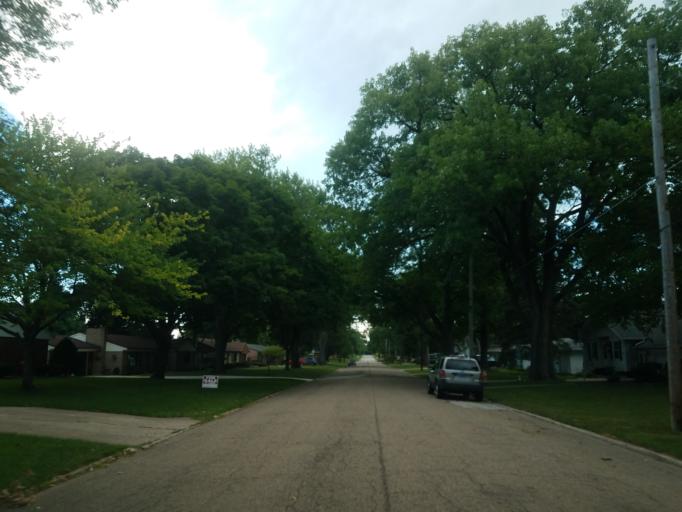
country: US
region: Illinois
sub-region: McLean County
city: Bloomington
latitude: 40.4694
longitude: -88.9653
